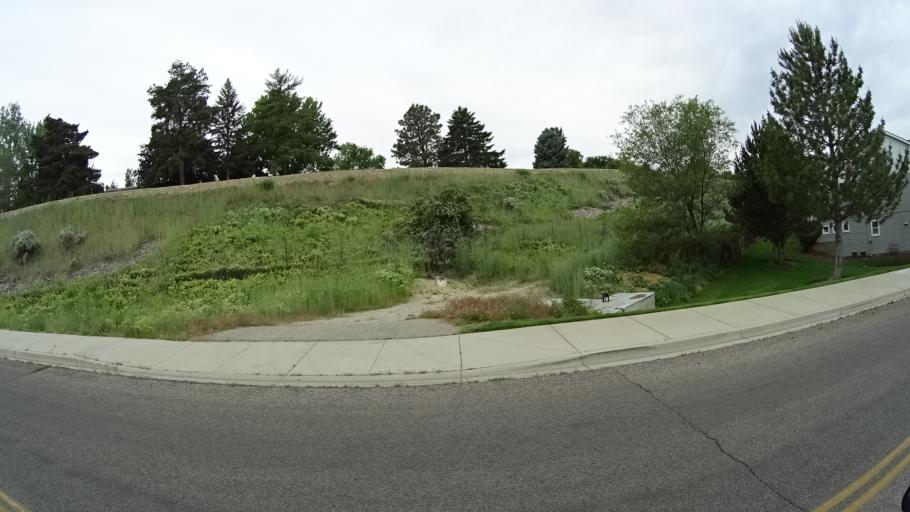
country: US
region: Idaho
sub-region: Ada County
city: Boise
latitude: 43.5791
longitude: -116.2240
